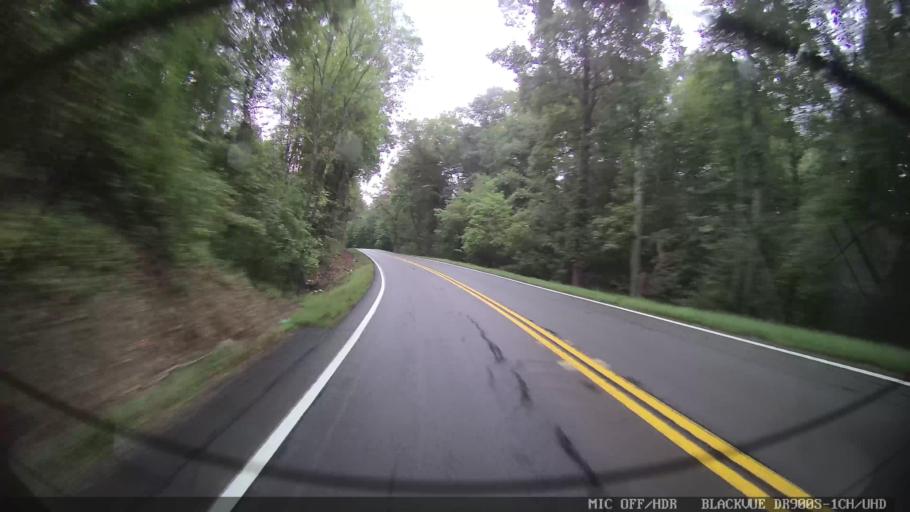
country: US
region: Georgia
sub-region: Gilmer County
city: Ellijay
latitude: 34.7410
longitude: -84.5269
